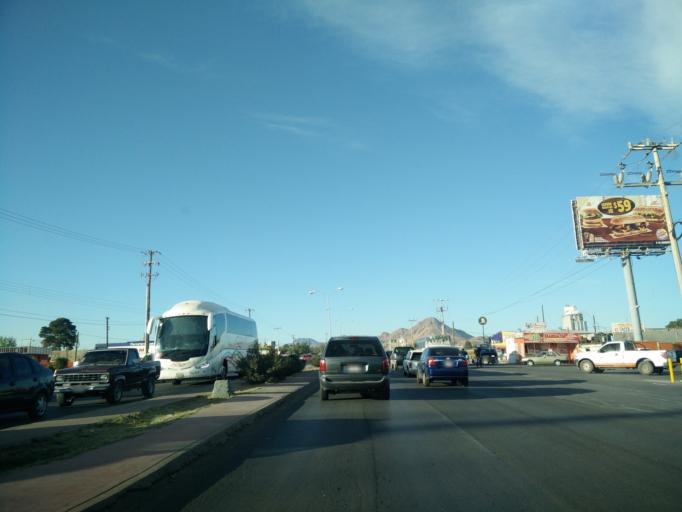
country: MX
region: Chihuahua
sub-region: Chihuahua
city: Chihuahua
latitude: 28.6452
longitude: -106.0141
